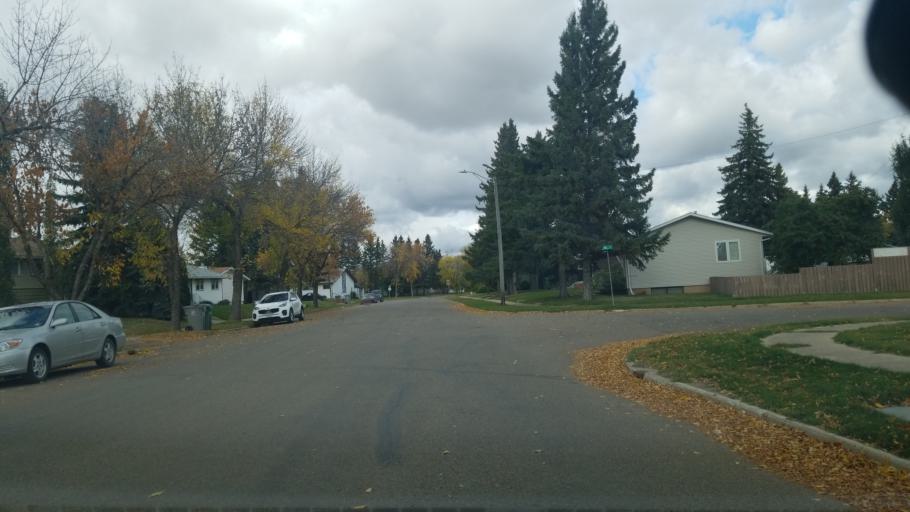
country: CA
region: Saskatchewan
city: Lloydminster
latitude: 53.2796
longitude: -110.0199
